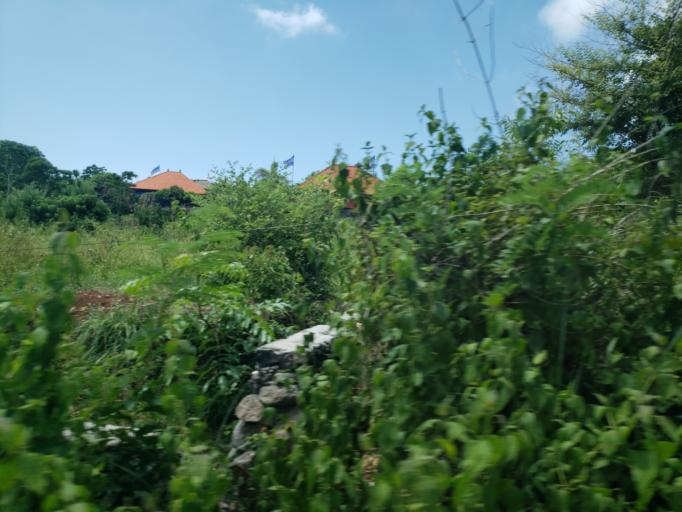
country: ID
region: Bali
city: Kangin
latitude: -8.8423
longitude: 115.1468
